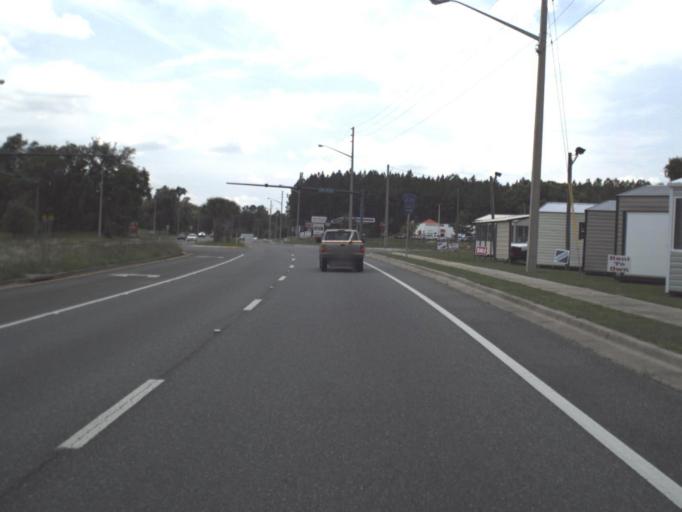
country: US
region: Florida
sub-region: Alachua County
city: Newberry
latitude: 29.6520
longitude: -82.5974
